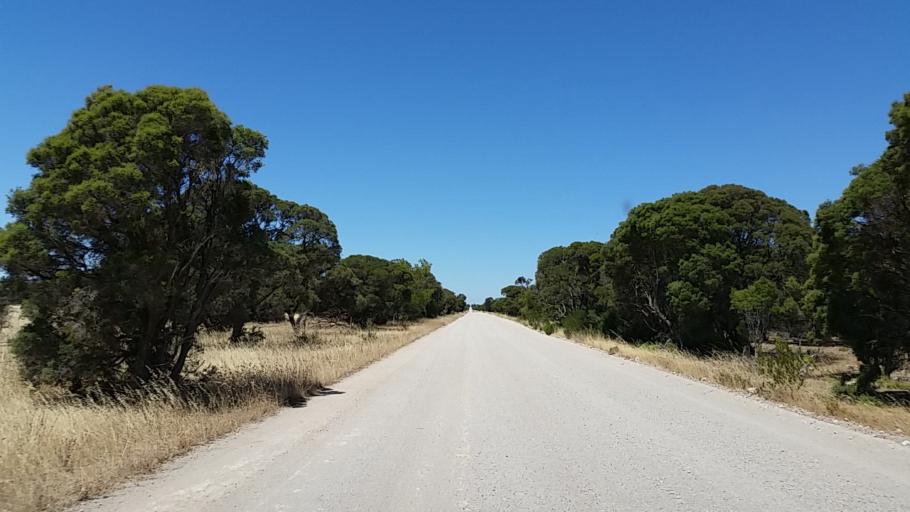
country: AU
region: South Australia
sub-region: Yorke Peninsula
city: Honiton
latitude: -35.0789
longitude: 137.4914
